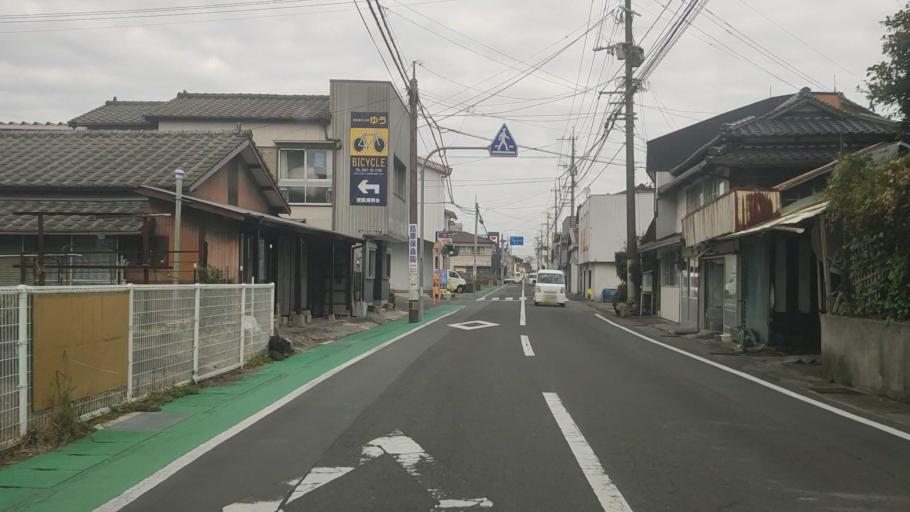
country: JP
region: Nagasaki
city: Shimabara
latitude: 32.7665
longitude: 130.3694
